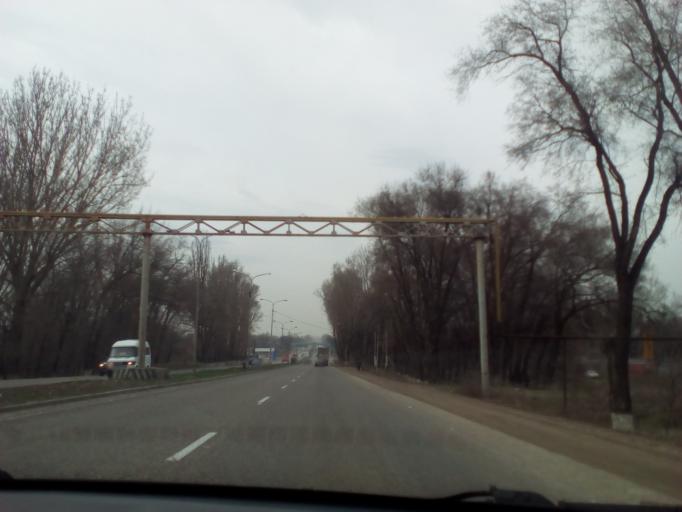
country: KZ
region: Almaty Oblysy
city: Burunday
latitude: 43.2169
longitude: 76.6586
